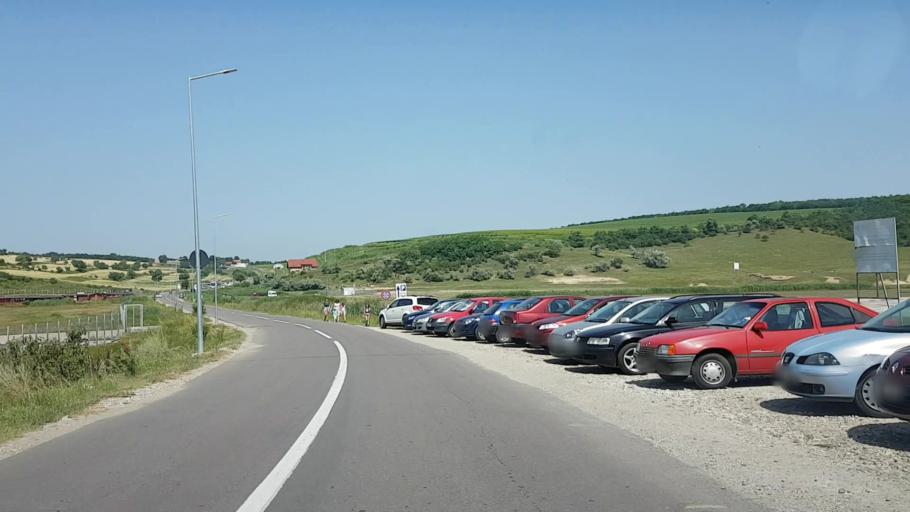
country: RO
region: Cluj
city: Turda
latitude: 46.5878
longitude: 23.7918
